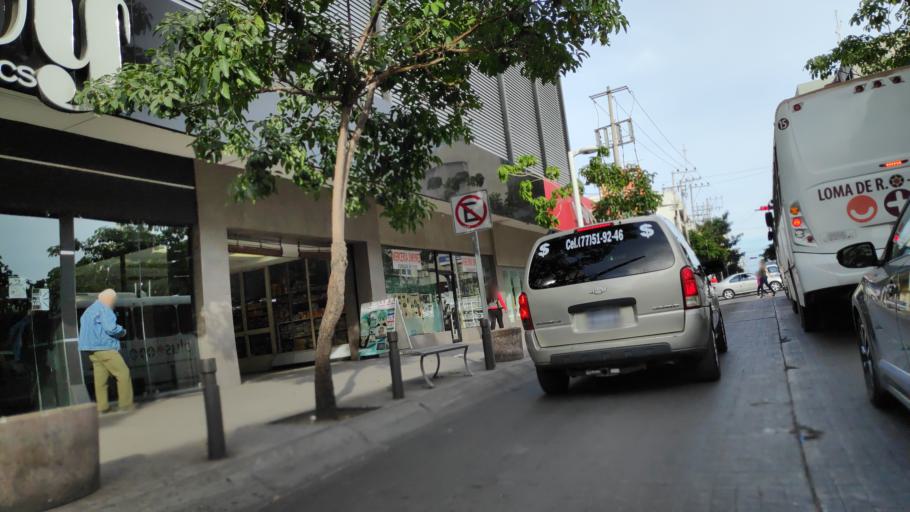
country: MX
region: Sinaloa
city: Culiacan
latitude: 24.8098
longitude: -107.3956
